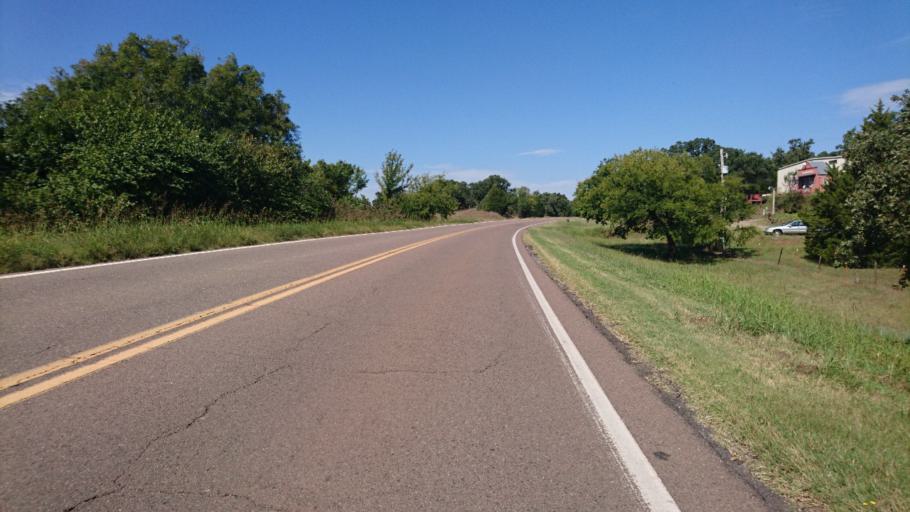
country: US
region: Oklahoma
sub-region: Oklahoma County
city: Jones
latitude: 35.6610
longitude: -97.2926
